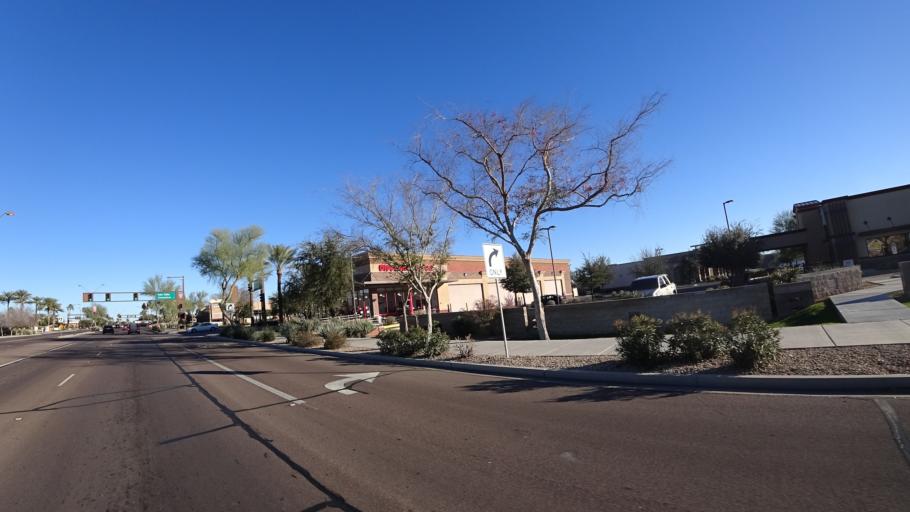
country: US
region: Arizona
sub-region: Maricopa County
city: Avondale
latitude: 33.4642
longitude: -112.3438
